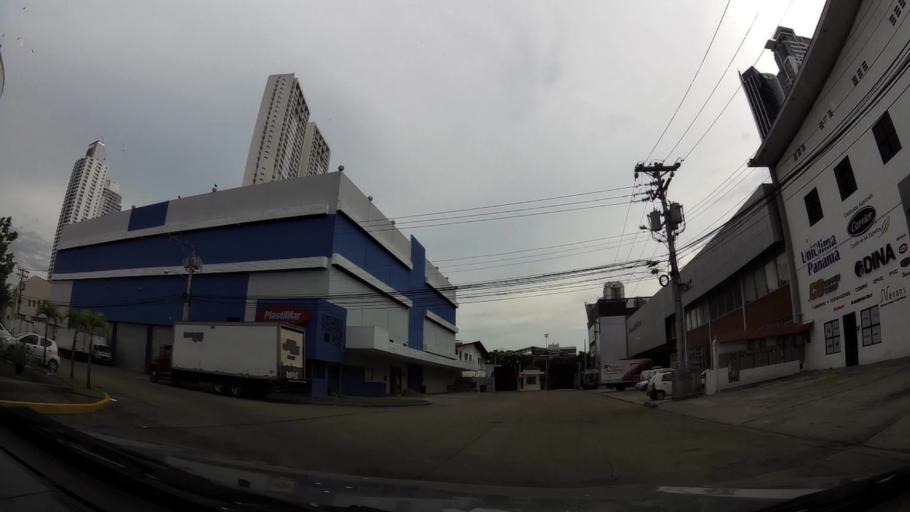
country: PA
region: Panama
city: San Miguelito
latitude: 9.0113
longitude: -79.4790
